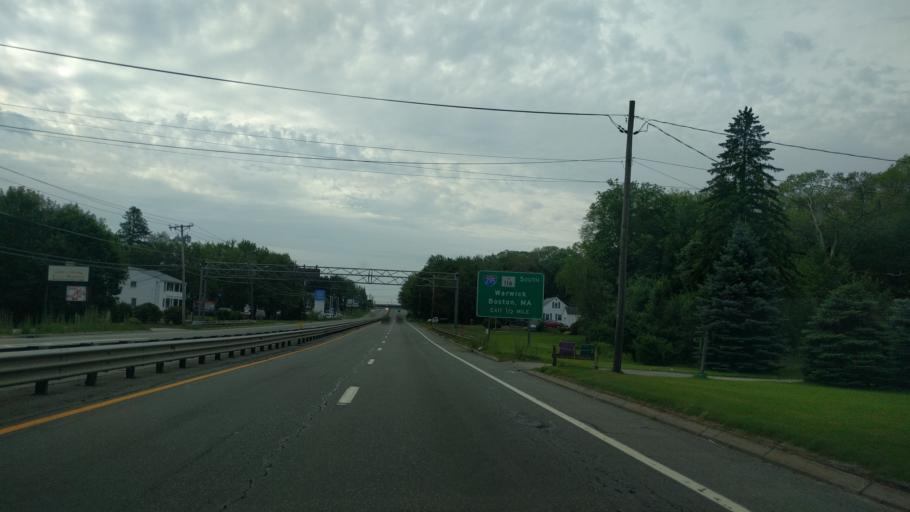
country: US
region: Rhode Island
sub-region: Providence County
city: Cumberland Hill
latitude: 41.9560
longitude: -71.4899
